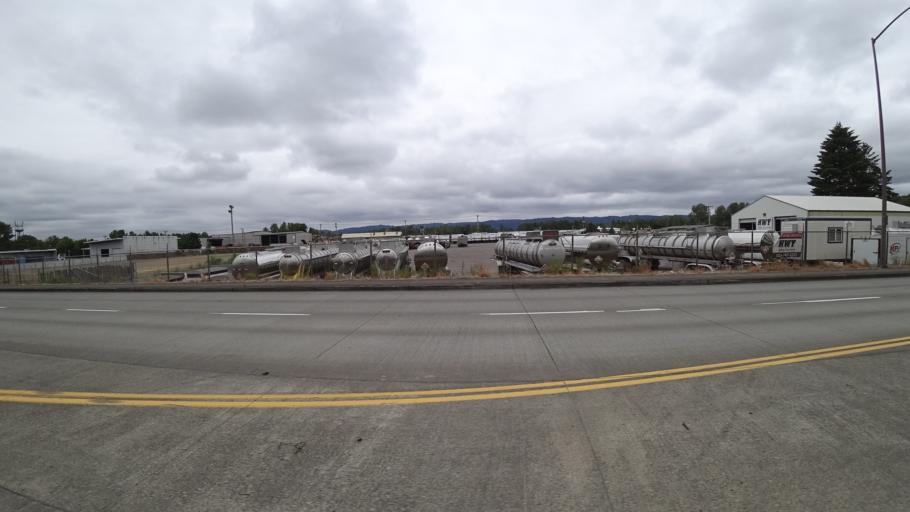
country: US
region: Washington
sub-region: Clark County
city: Vancouver
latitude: 45.6159
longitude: -122.7096
